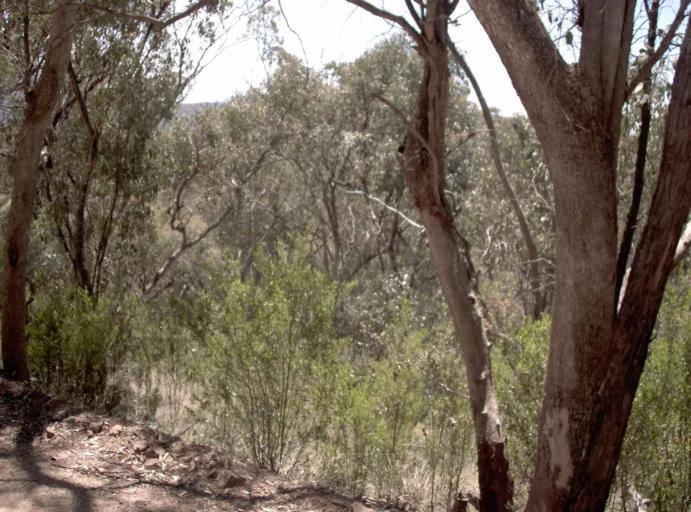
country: AU
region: New South Wales
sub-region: Snowy River
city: Jindabyne
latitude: -36.9764
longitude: 148.3016
